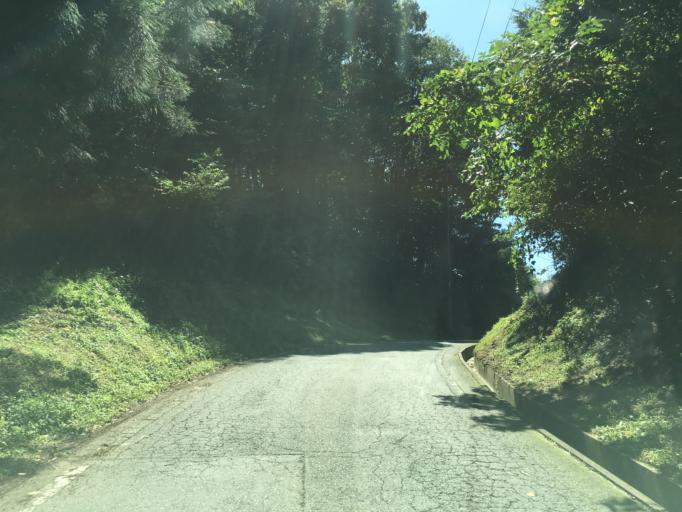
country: JP
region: Fukushima
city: Ishikawa
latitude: 37.2055
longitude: 140.5765
